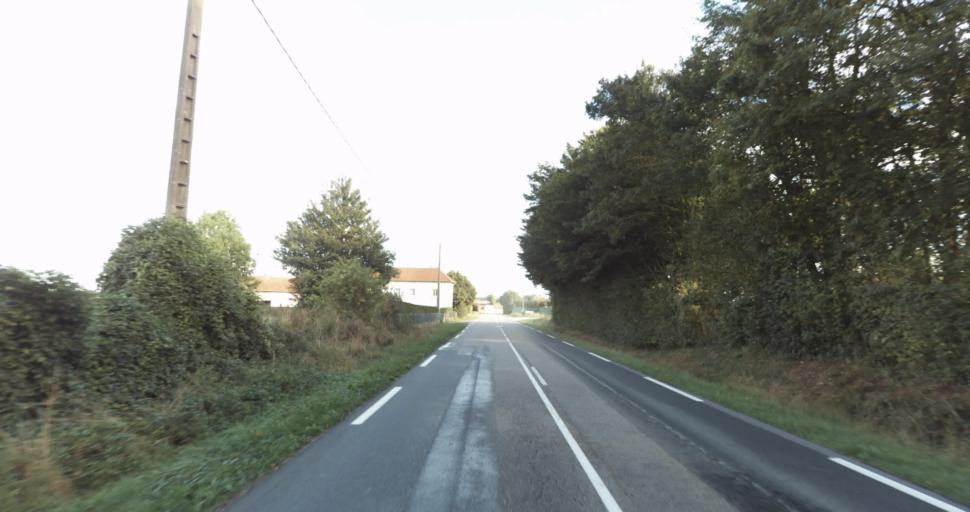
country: FR
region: Lower Normandy
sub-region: Departement de l'Orne
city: Sainte-Gauburge-Sainte-Colombe
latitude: 48.7346
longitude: 0.3982
